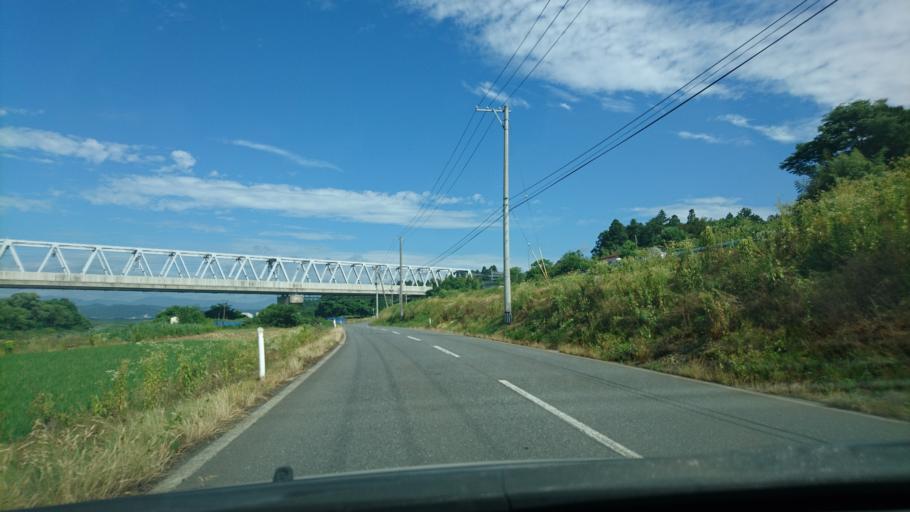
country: JP
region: Iwate
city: Ichinoseki
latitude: 38.9746
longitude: 141.1586
